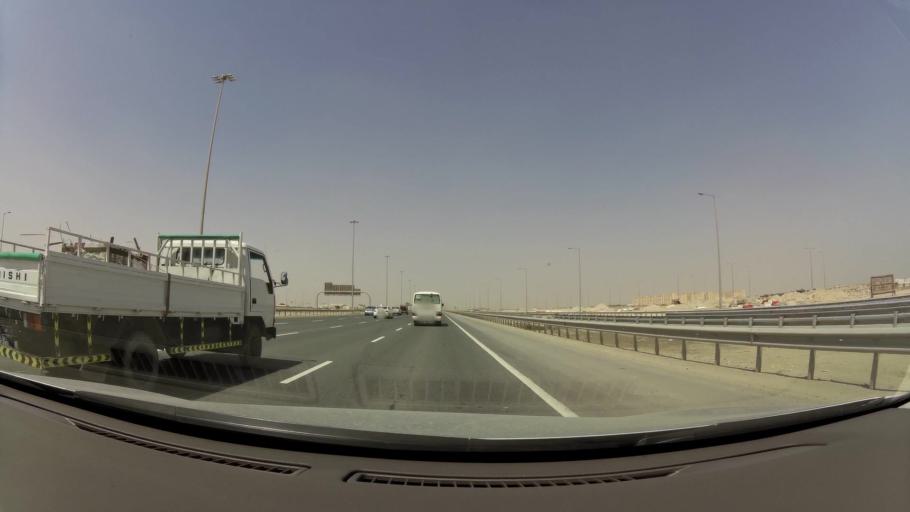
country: QA
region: Baladiyat Umm Salal
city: Umm Salal Muhammad
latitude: 25.4133
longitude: 51.4236
